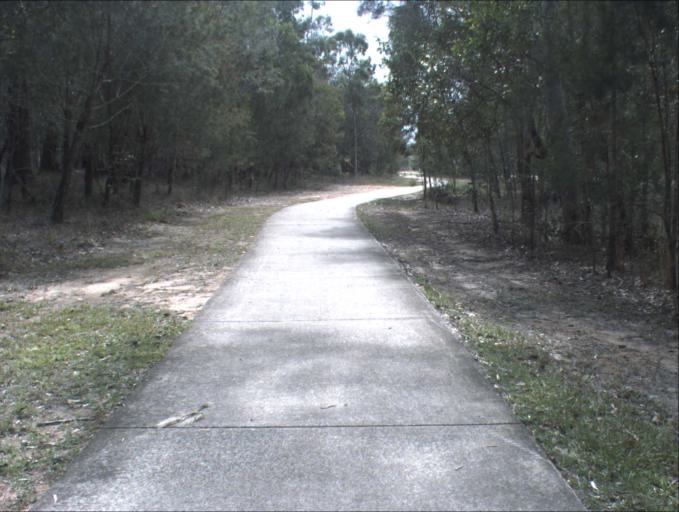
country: AU
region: Queensland
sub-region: Logan
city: Logan Reserve
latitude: -27.6776
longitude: 153.0691
